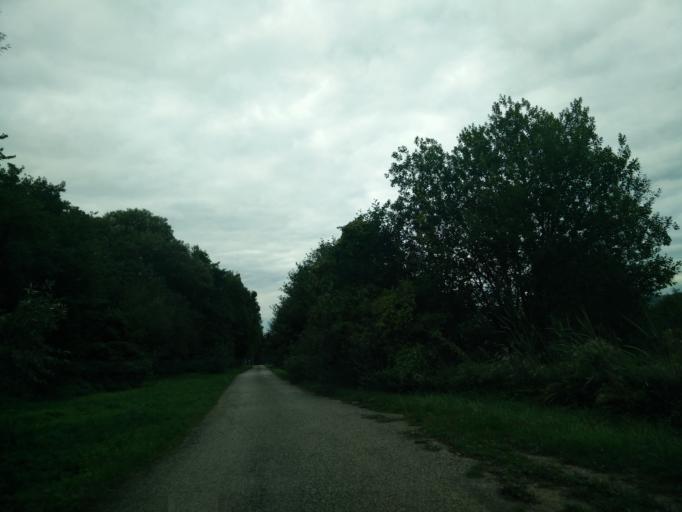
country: SK
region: Nitriansky
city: Novaky
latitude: 48.6368
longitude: 18.4915
